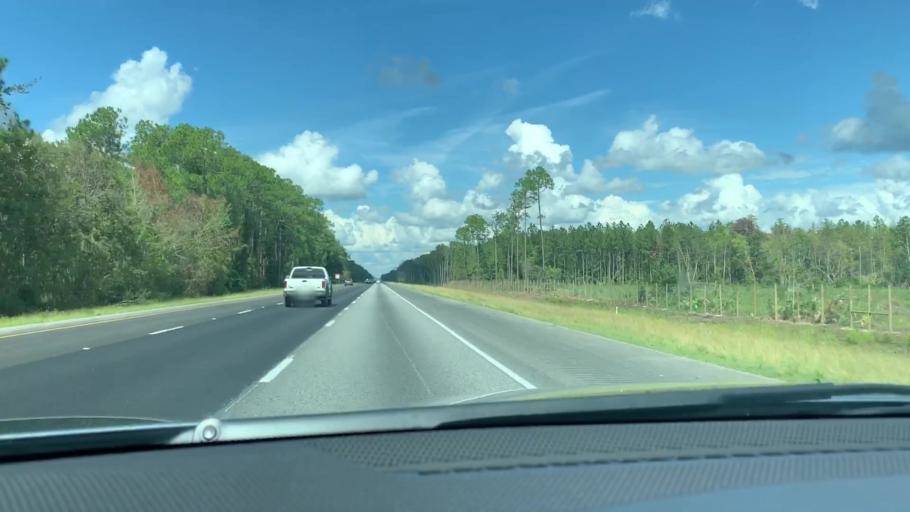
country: US
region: Georgia
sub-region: Camden County
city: Kingsland
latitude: 30.8829
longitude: -81.6857
